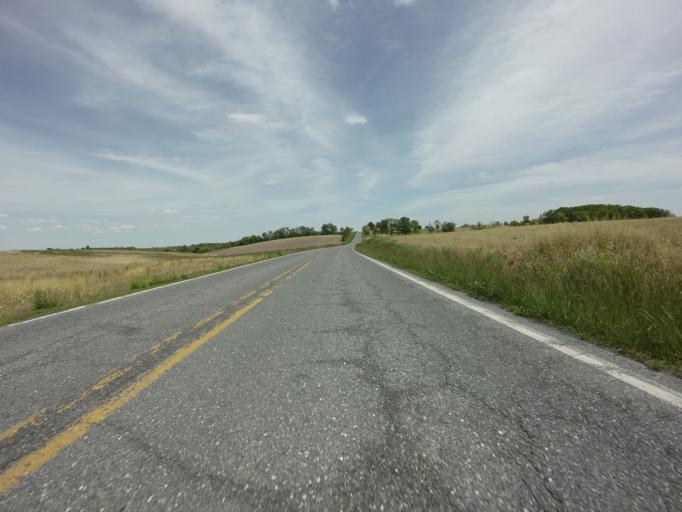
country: US
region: Maryland
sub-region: Frederick County
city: Woodsboro
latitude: 39.5149
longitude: -77.2425
